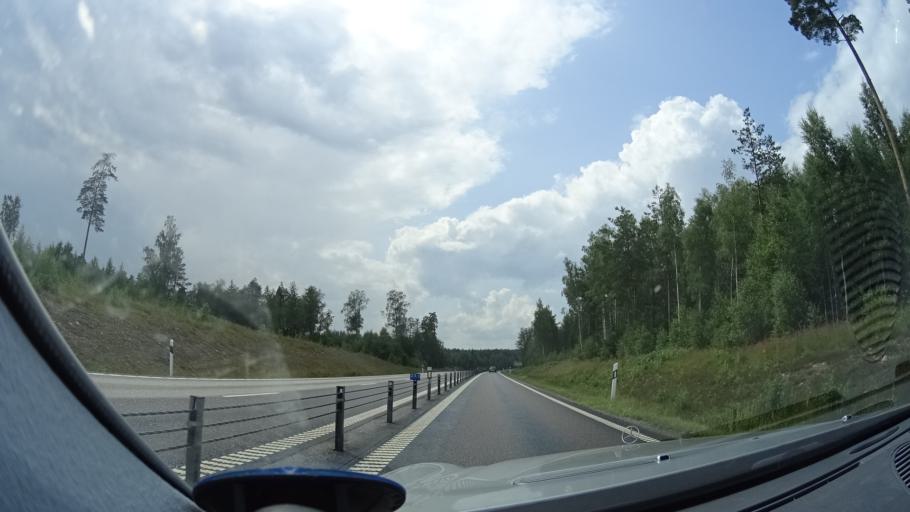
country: SE
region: Kalmar
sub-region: Nybro Kommun
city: Nybro
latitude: 56.7091
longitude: 15.7593
